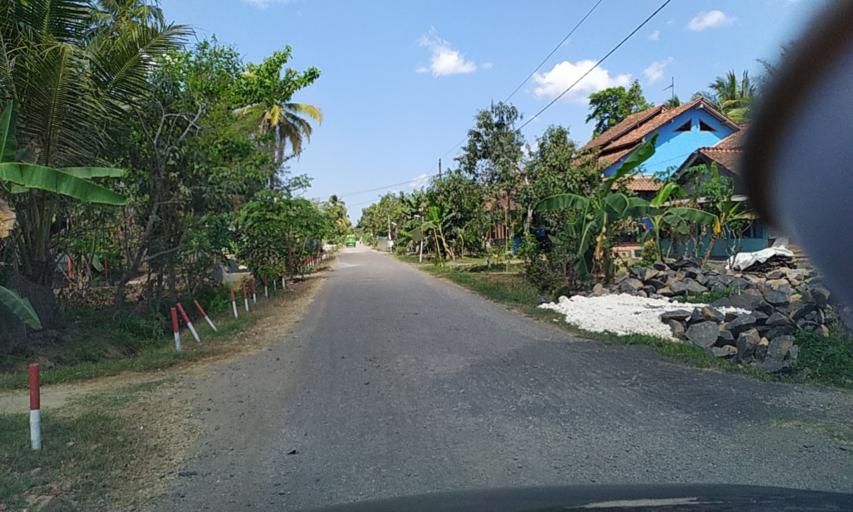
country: ID
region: Central Java
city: Kalenaren
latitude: -7.5812
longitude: 108.7885
